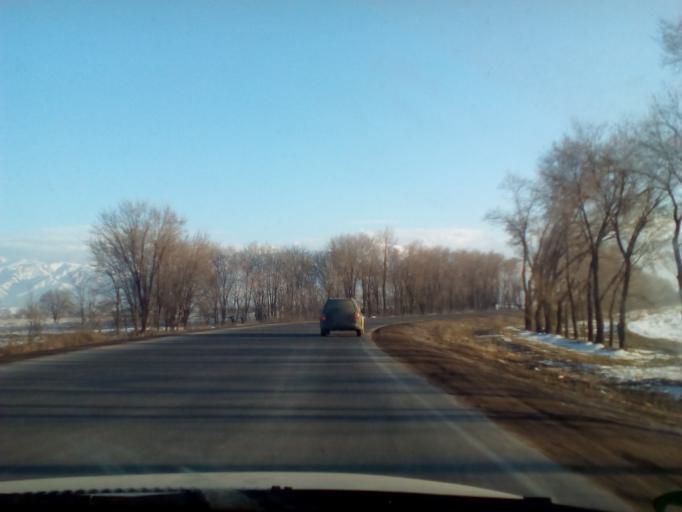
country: KZ
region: Almaty Oblysy
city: Burunday
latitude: 43.2146
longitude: 76.4143
